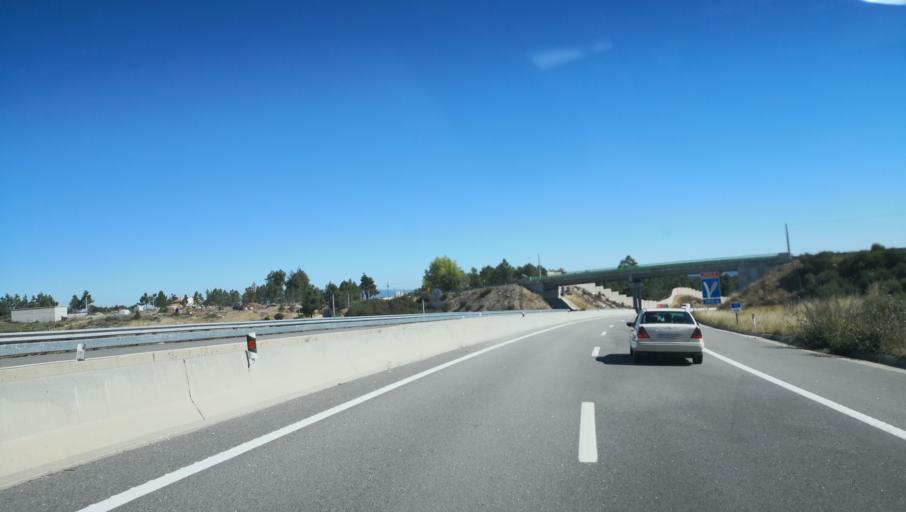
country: PT
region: Vila Real
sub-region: Murca
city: Murca
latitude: 41.3827
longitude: -7.5085
